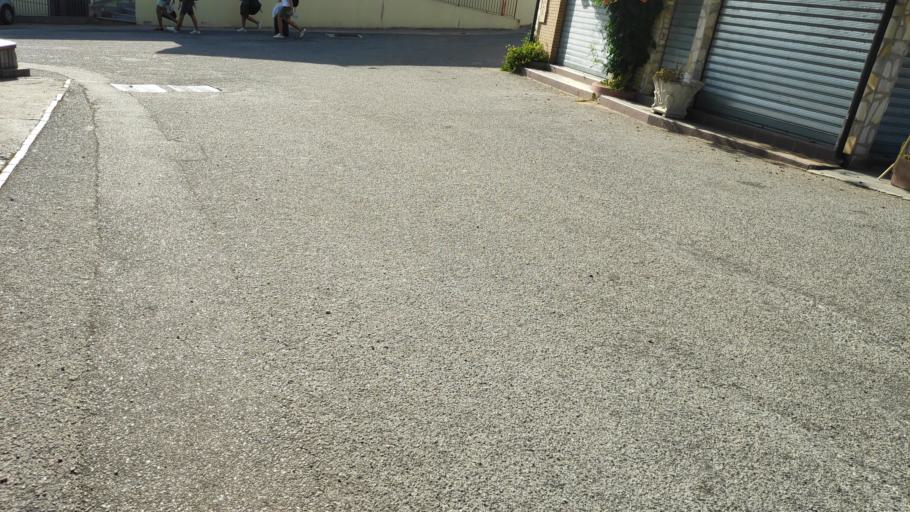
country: IT
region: Calabria
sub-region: Provincia di Catanzaro
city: Sant'Andrea Apostolo dello Ionio
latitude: 38.6231
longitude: 16.5283
